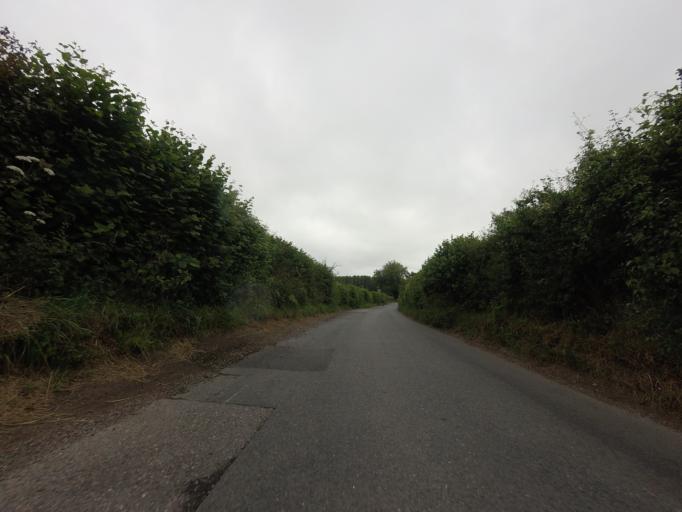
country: GB
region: England
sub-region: Kent
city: Borough Green
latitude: 51.3080
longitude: 0.2820
